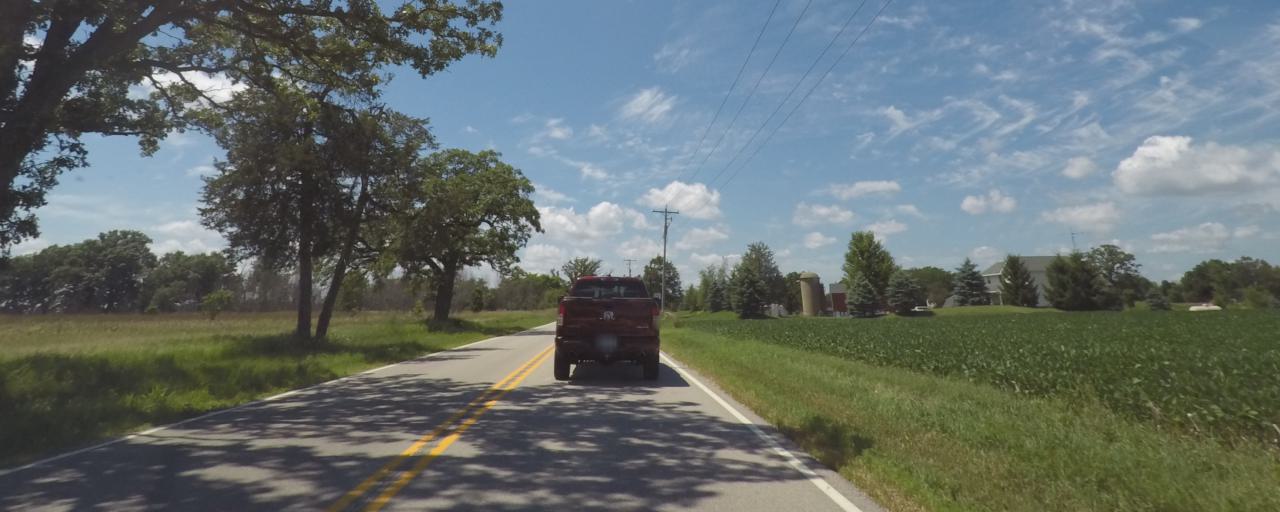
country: US
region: Wisconsin
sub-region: Waukesha County
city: Eagle
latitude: 42.9264
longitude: -88.5280
